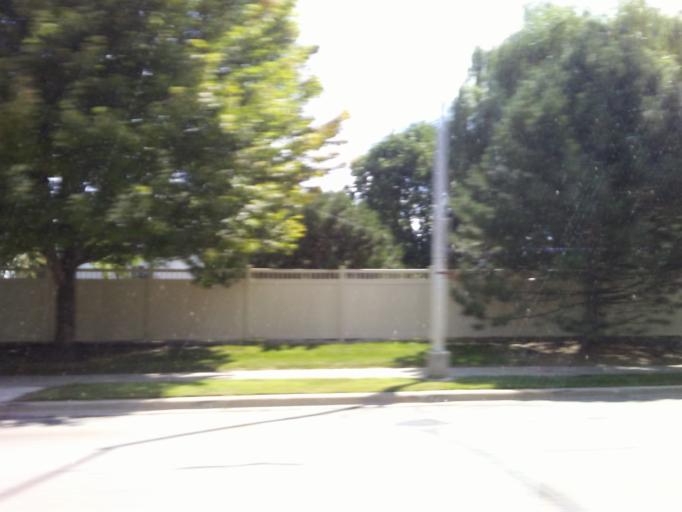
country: US
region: Wisconsin
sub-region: Dane County
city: Verona
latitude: 43.0390
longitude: -89.5182
